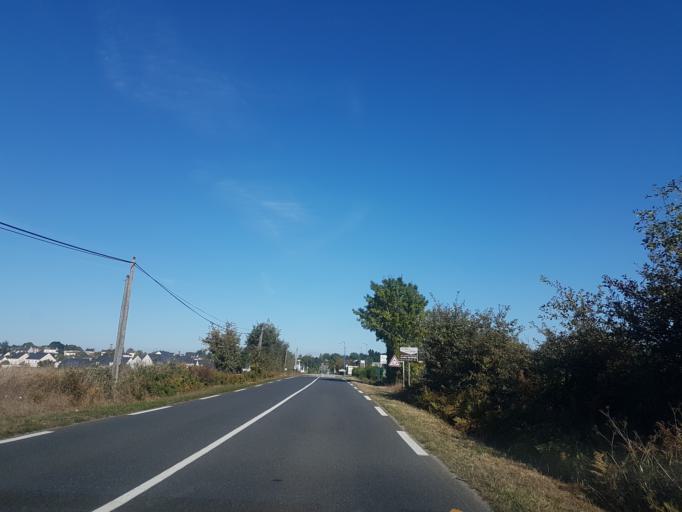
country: FR
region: Pays de la Loire
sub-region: Departement de la Loire-Atlantique
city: Nort-sur-Erdre
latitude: 47.4347
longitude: -1.4827
